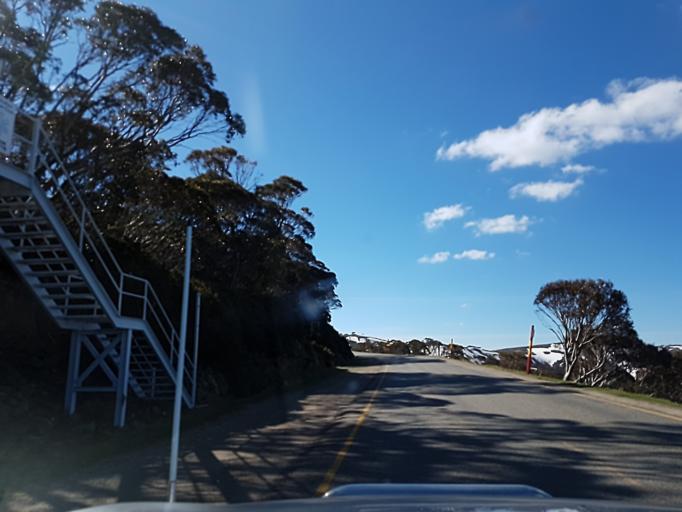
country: AU
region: Victoria
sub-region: Alpine
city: Mount Beauty
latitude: -36.9866
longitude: 147.1476
